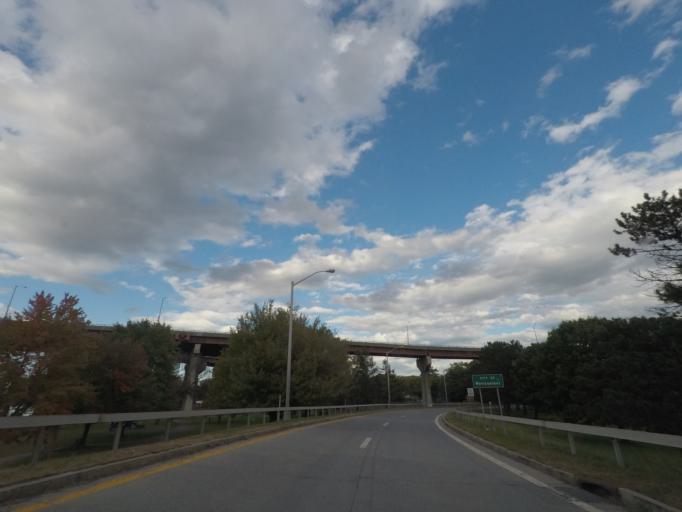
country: US
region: New York
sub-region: Rensselaer County
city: Rensselaer
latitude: 42.6417
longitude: -73.7466
